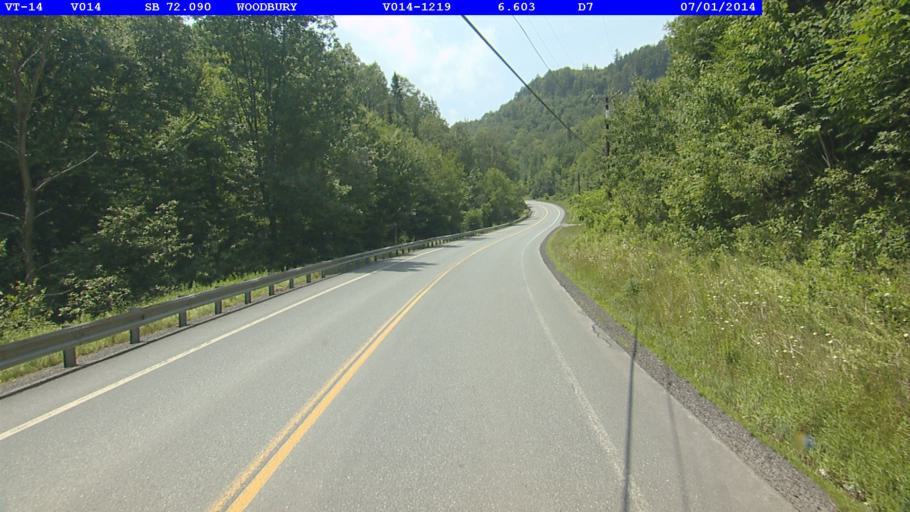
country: US
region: Vermont
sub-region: Caledonia County
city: Hardwick
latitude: 44.4746
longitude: -72.3963
